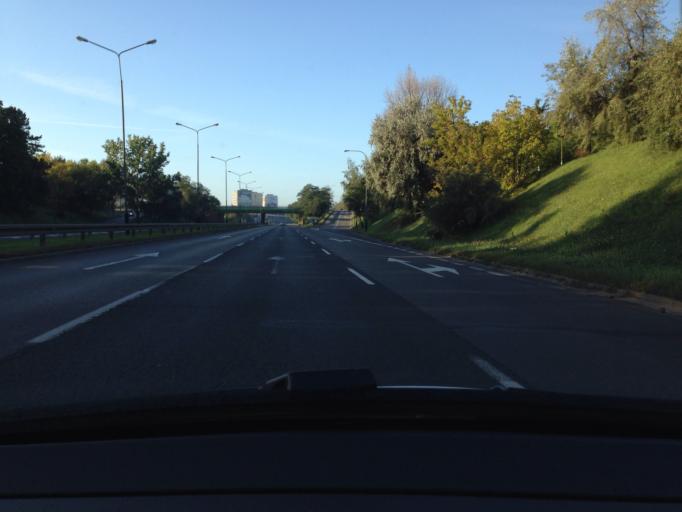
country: PL
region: Greater Poland Voivodeship
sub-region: Poznan
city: Poznan
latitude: 52.4373
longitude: 16.9081
